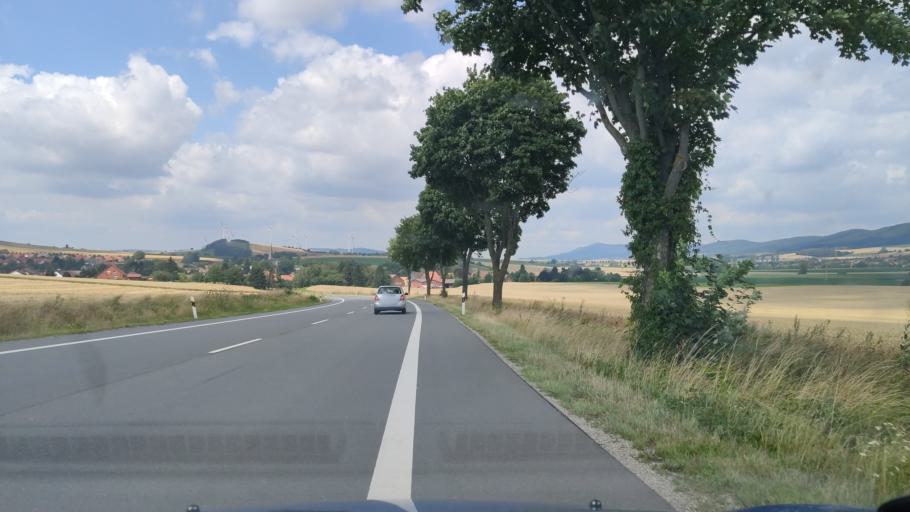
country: DE
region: Lower Saxony
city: Halle
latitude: 51.9855
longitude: 9.5718
